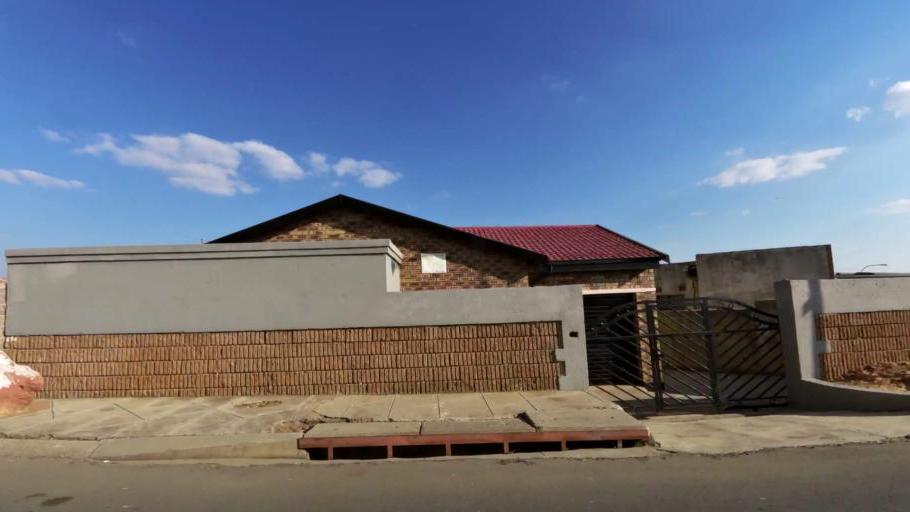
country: ZA
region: Gauteng
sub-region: City of Johannesburg Metropolitan Municipality
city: Roodepoort
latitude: -26.2023
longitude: 27.8805
